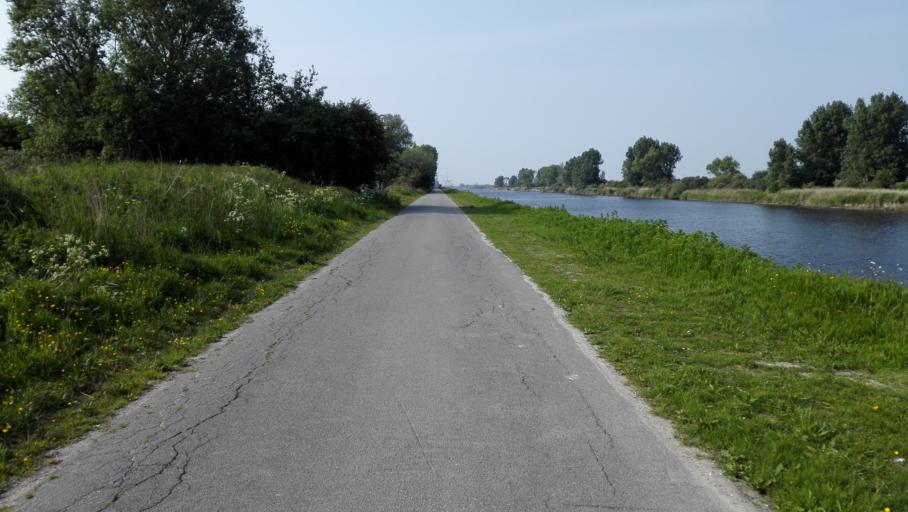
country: BE
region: Flanders
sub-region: Provincie West-Vlaanderen
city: Zeebrugge
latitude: 51.2959
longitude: 3.2057
